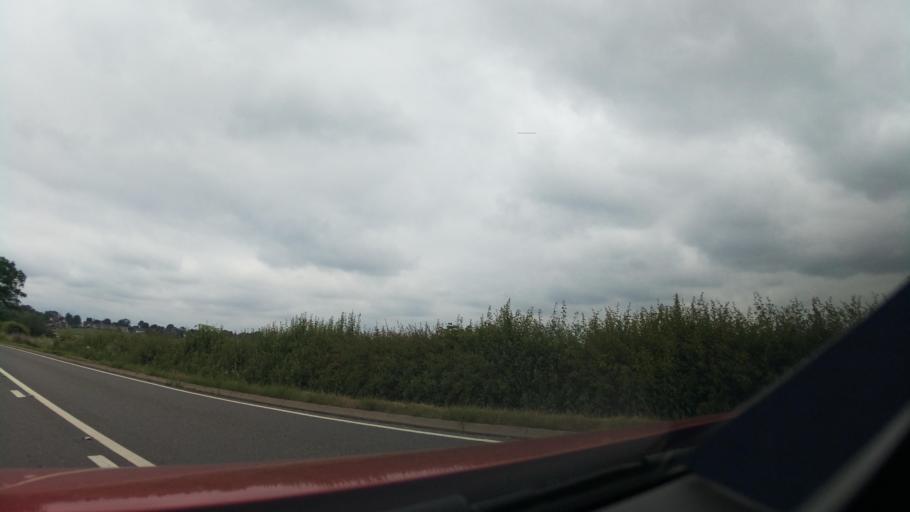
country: GB
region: England
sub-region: Leicestershire
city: Melton Mowbray
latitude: 52.7350
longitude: -0.8509
